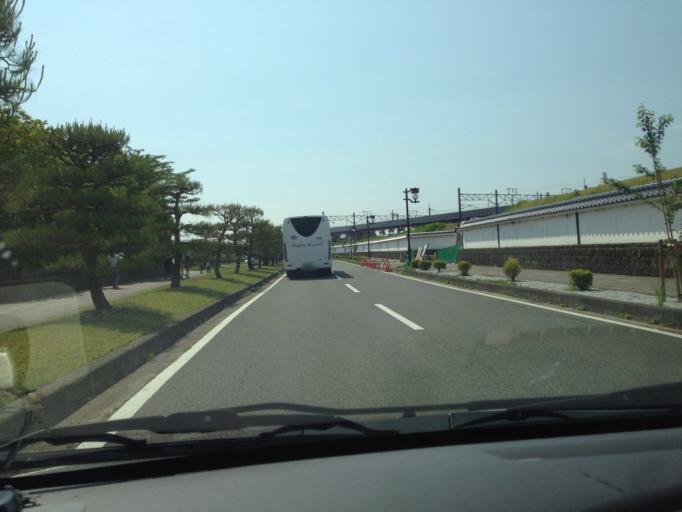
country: JP
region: Fukushima
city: Sukagawa
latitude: 37.1313
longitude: 140.2118
